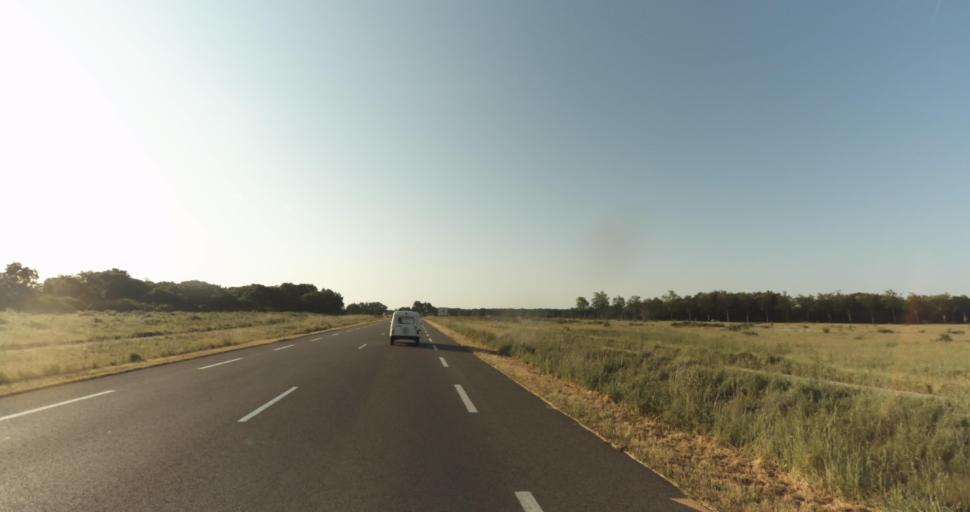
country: FR
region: Midi-Pyrenees
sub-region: Departement de la Haute-Garonne
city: Fontenilles
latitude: 43.5275
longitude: 1.2020
